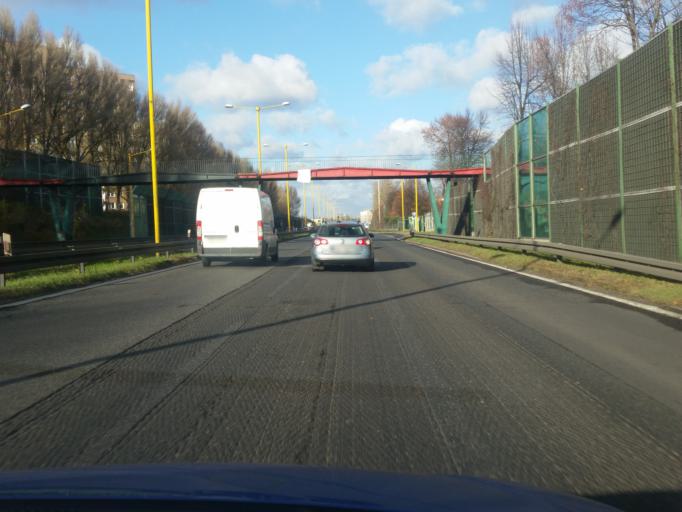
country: PL
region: Silesian Voivodeship
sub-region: Czestochowa
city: Czestochowa
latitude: 50.7755
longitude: 19.1523
